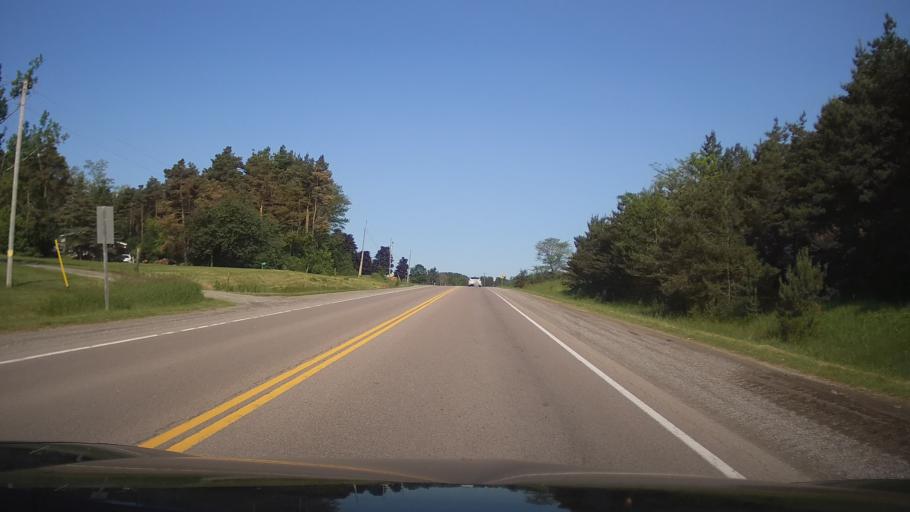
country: CA
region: Ontario
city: Omemee
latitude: 44.3475
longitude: -78.7806
